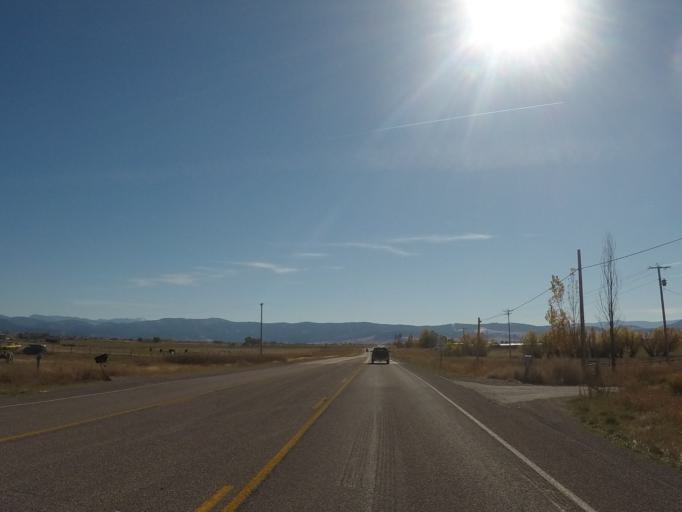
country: US
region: Montana
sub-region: Lake County
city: Ronan
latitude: 47.3821
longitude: -114.0967
